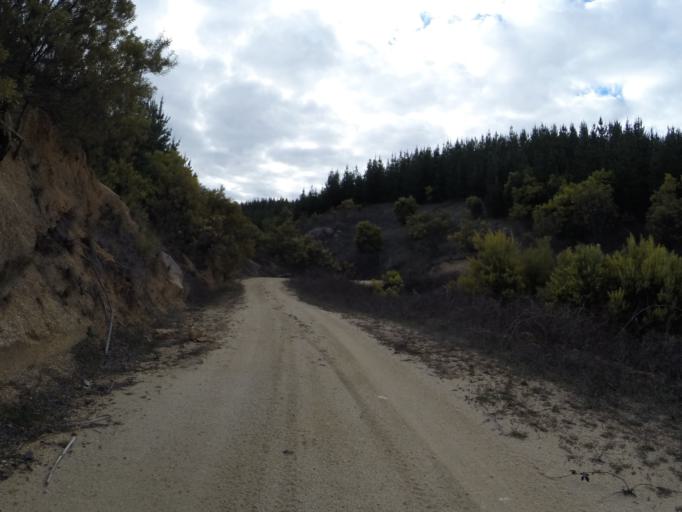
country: AU
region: Australian Capital Territory
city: Macquarie
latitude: -35.3502
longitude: 148.9498
